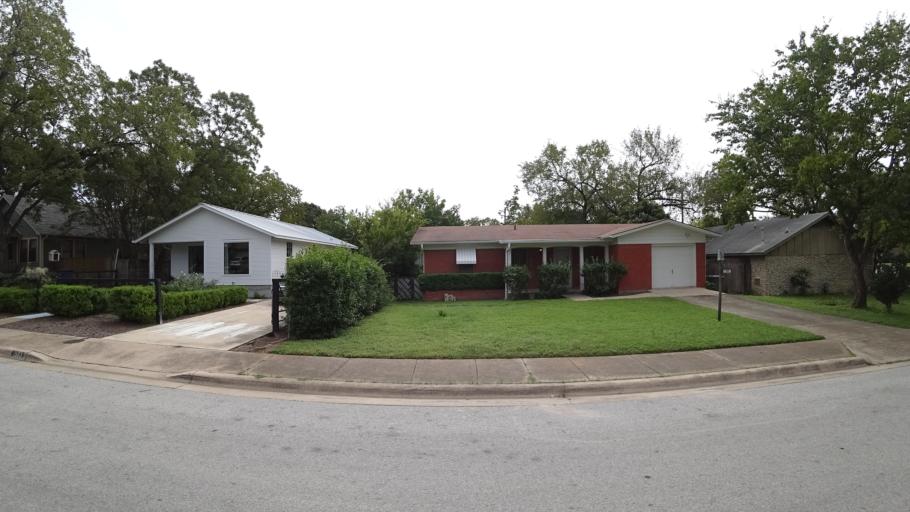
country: US
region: Texas
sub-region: Travis County
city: Austin
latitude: 30.2723
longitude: -97.7232
